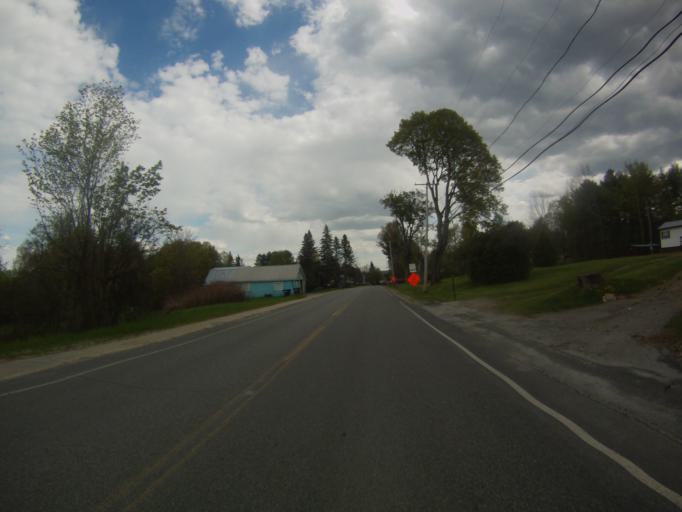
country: US
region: New York
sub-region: Essex County
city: Mineville
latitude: 44.0826
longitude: -73.5291
